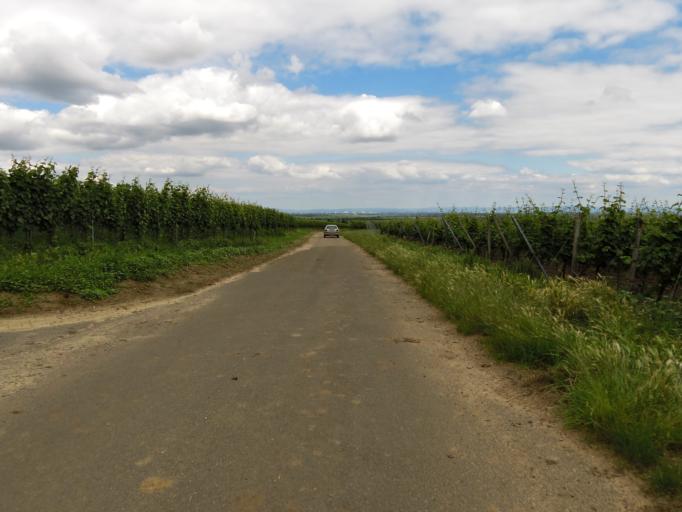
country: DE
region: Rheinland-Pfalz
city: Kallstadt
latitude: 49.4847
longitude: 8.1731
